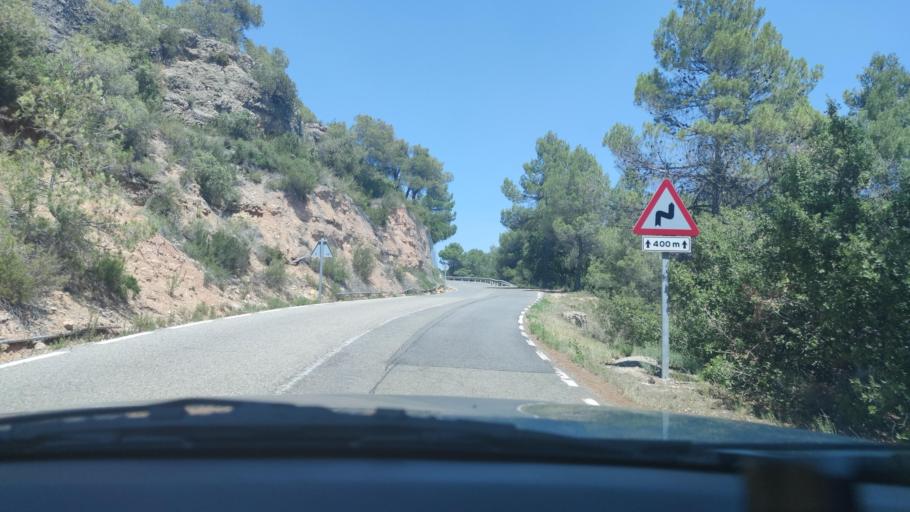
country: ES
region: Catalonia
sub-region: Provincia de Tarragona
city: Vilanova de Prades
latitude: 41.3756
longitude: 0.9383
